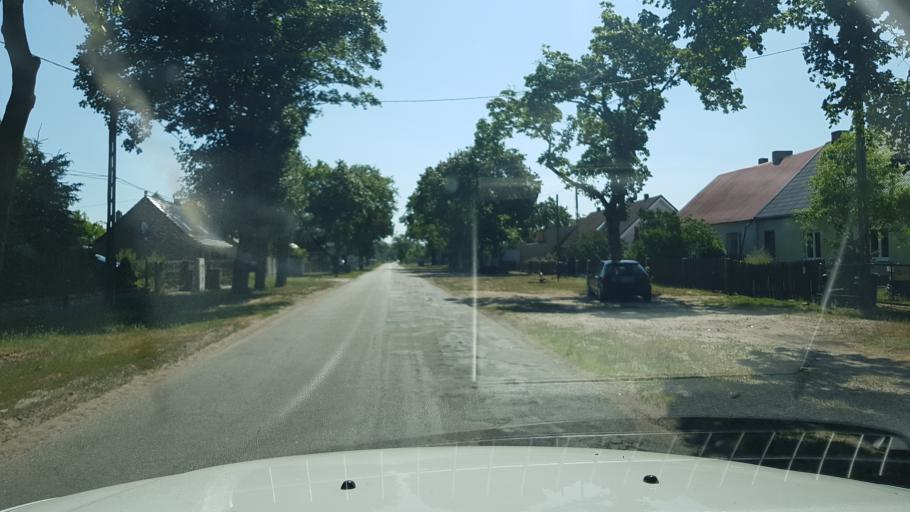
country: PL
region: West Pomeranian Voivodeship
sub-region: Powiat goleniowski
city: Goleniow
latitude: 53.4586
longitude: 14.7208
